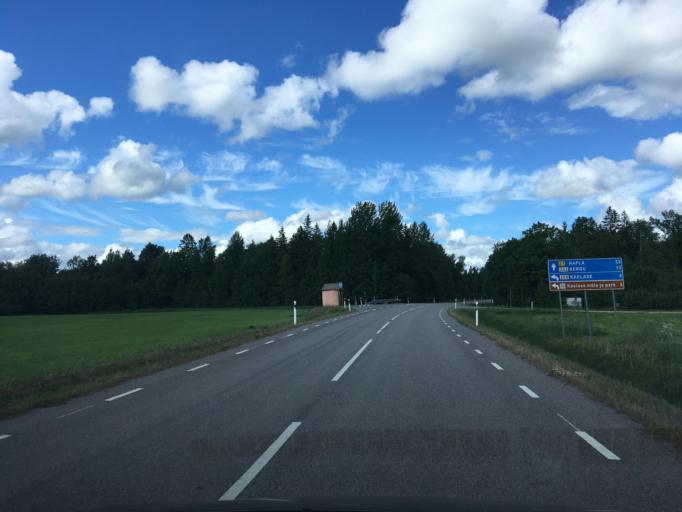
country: EE
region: Paernumaa
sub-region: Halinga vald
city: Parnu-Jaagupi
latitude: 58.6639
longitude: 24.5800
